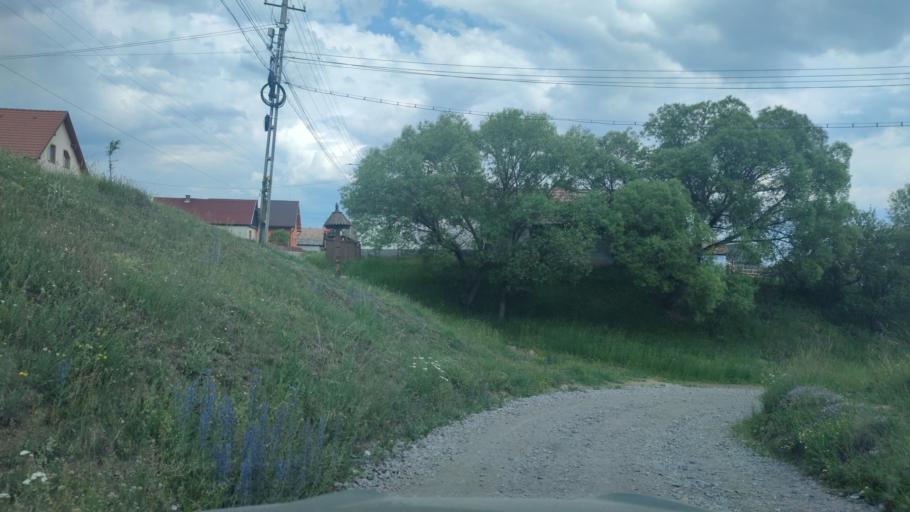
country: RO
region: Harghita
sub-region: Comuna Remetea
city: Remetea
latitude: 46.7953
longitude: 25.4458
